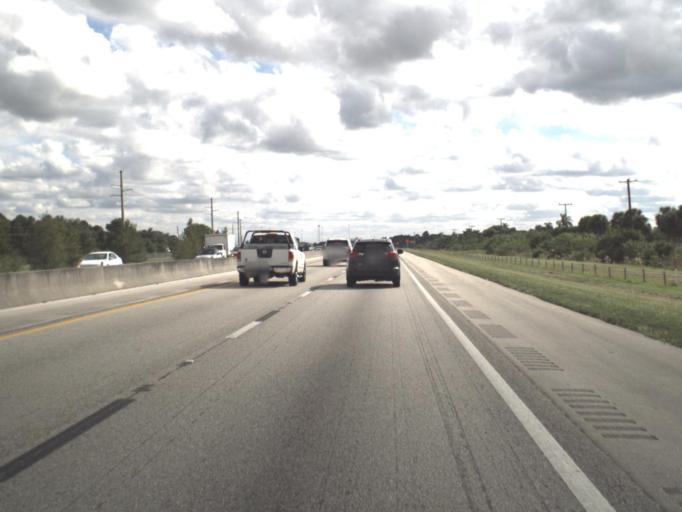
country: US
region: Florida
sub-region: Saint Lucie County
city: River Park
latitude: 27.3159
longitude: -80.3744
